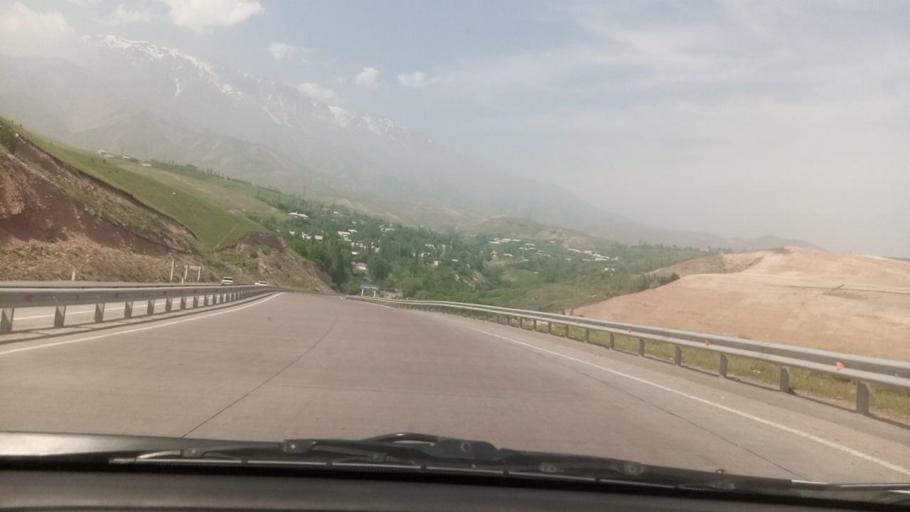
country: UZ
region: Toshkent
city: Angren
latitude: 41.0687
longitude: 70.2325
